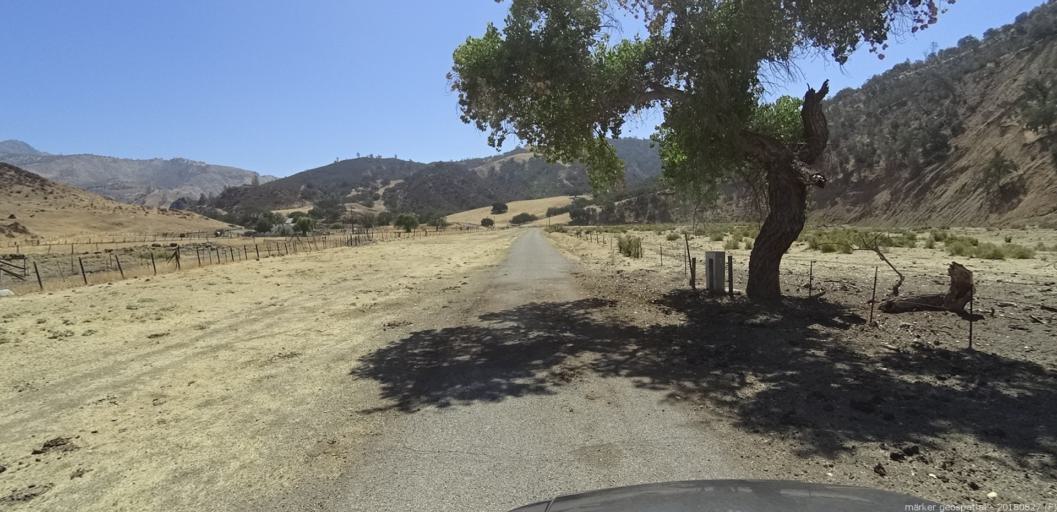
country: US
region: California
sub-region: Monterey County
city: King City
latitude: 36.2925
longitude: -120.8912
